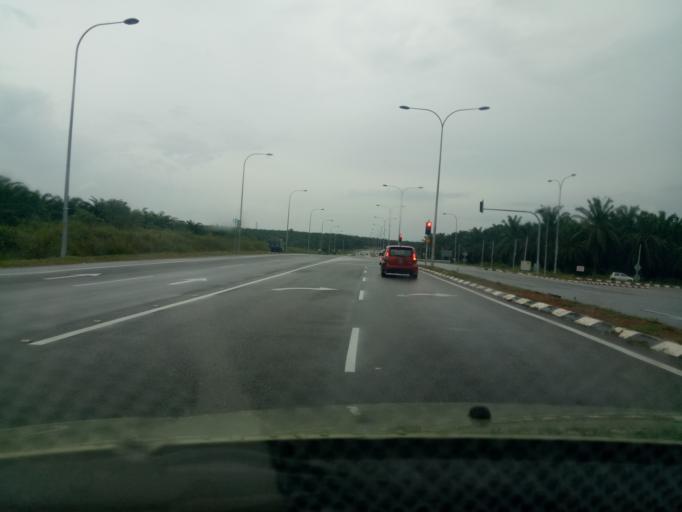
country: MY
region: Kedah
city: Sungai Petani
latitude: 5.6116
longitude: 100.5678
